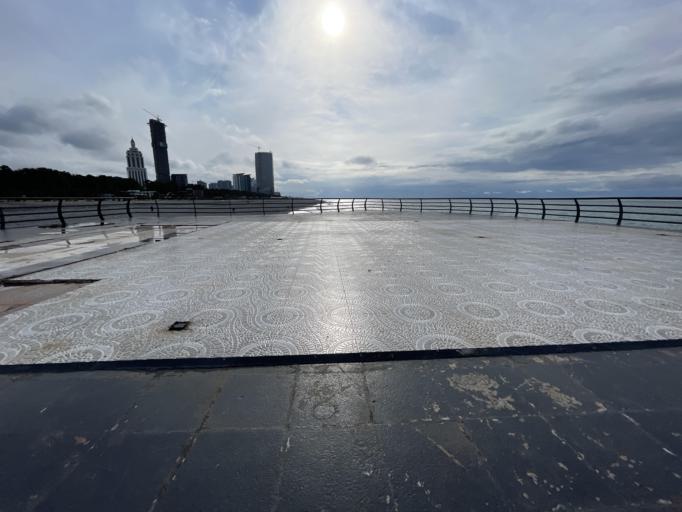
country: GE
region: Ajaria
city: Batumi
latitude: 41.6565
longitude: 41.6332
